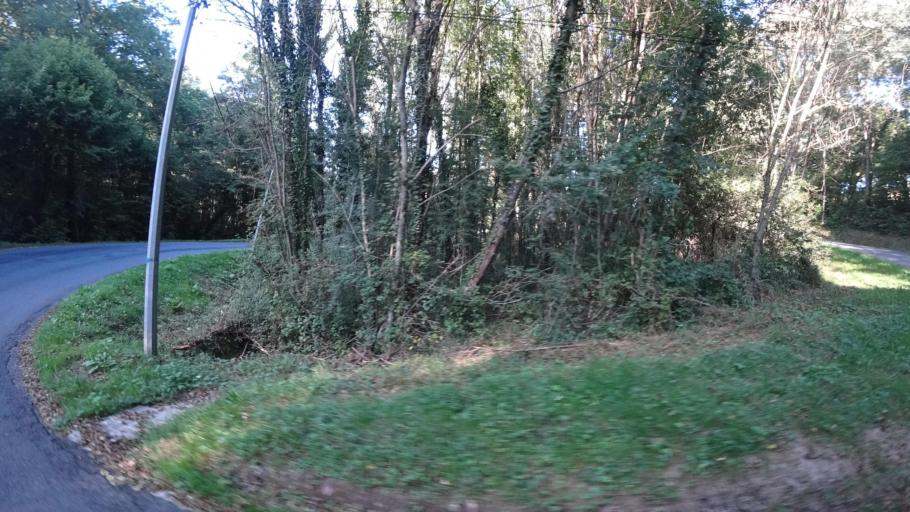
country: FR
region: Midi-Pyrenees
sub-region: Departement de l'Aveyron
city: Firmi
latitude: 44.5311
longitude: 2.3168
